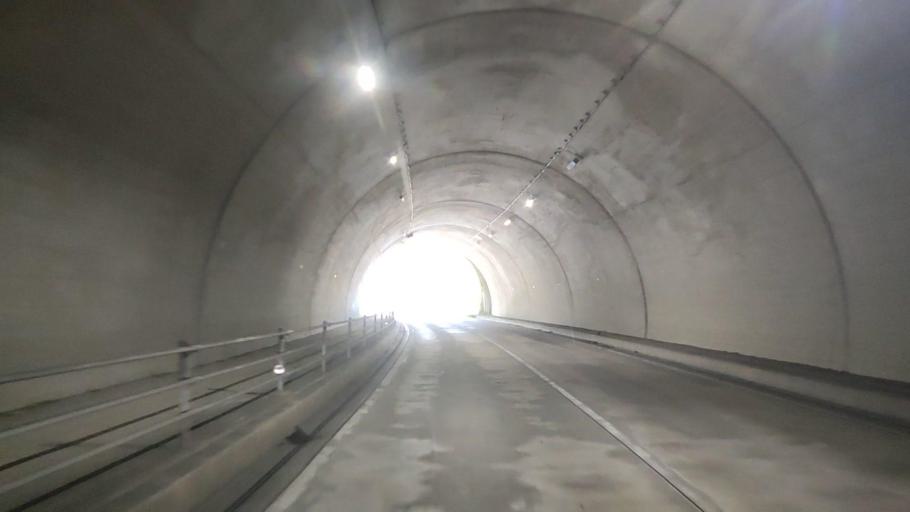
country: JP
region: Gifu
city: Godo
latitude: 35.5587
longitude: 136.6412
